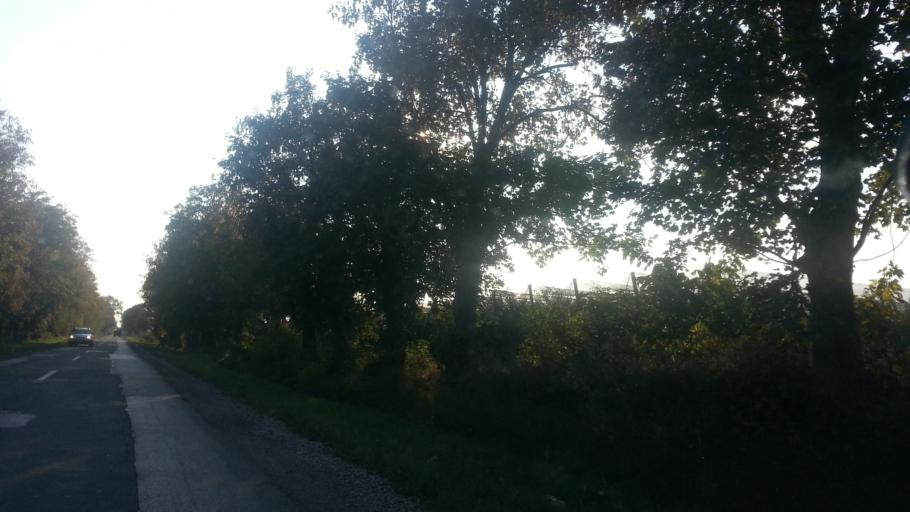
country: RS
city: Novi Slankamen
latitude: 45.1062
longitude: 20.2132
